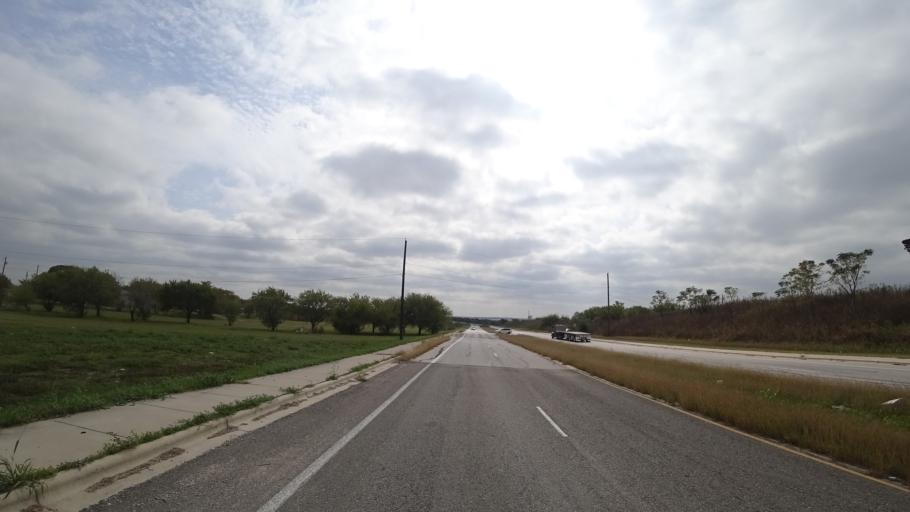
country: US
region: Texas
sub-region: Travis County
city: Pflugerville
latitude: 30.3847
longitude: -97.6141
